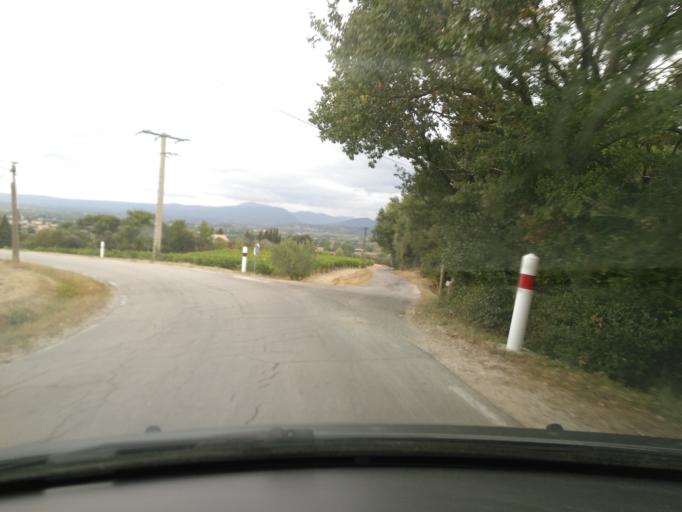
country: FR
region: Provence-Alpes-Cote d'Azur
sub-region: Departement du Vaucluse
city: Valreas
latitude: 44.3733
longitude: 5.0110
